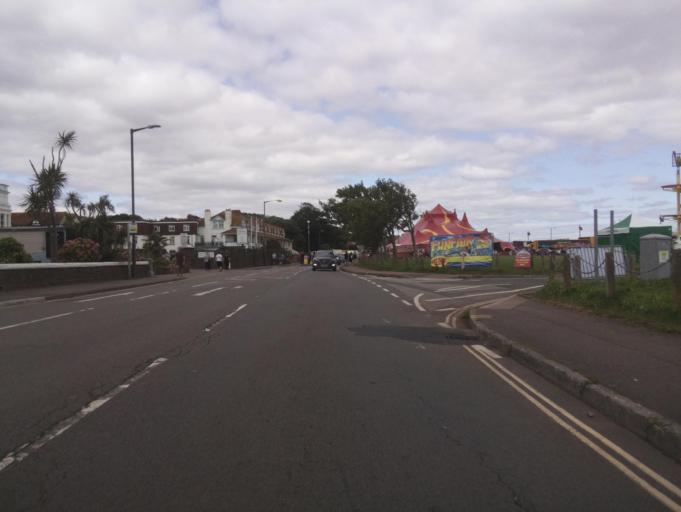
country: GB
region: England
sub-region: Borough of Torbay
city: Paignton
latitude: 50.4376
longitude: -3.5602
